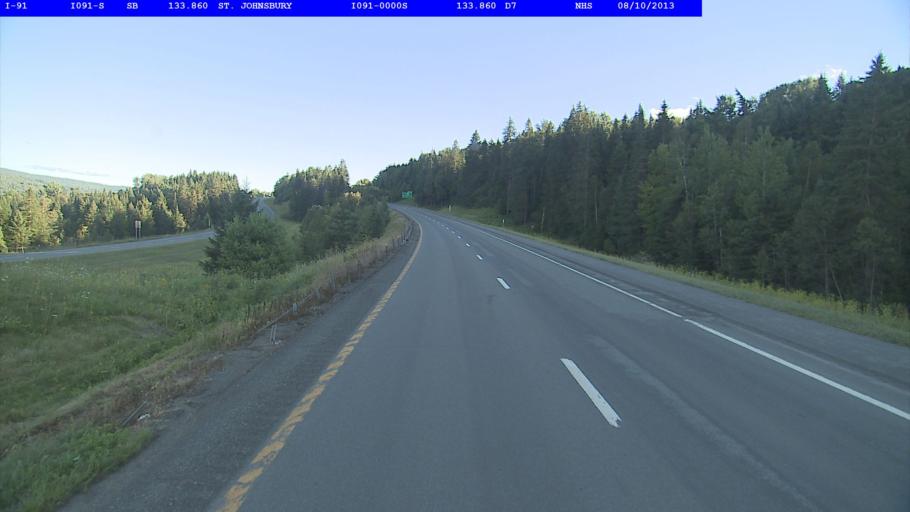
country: US
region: Vermont
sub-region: Caledonia County
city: Lyndon
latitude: 44.4728
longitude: -72.0254
